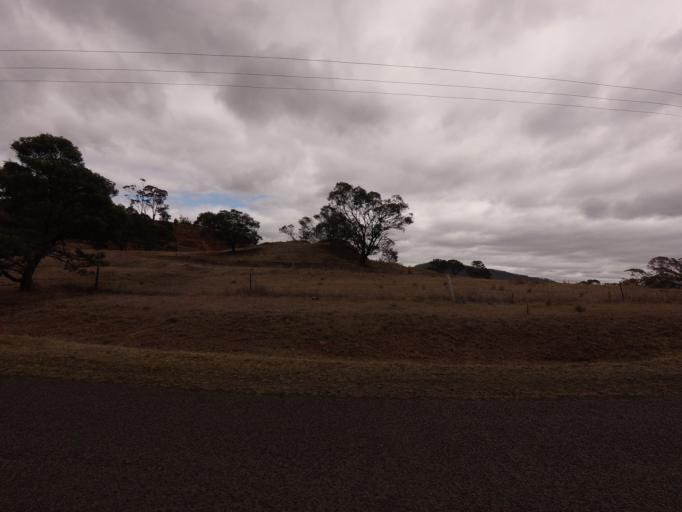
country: AU
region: Tasmania
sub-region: Clarence
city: Cambridge
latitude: -42.7912
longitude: 147.4025
